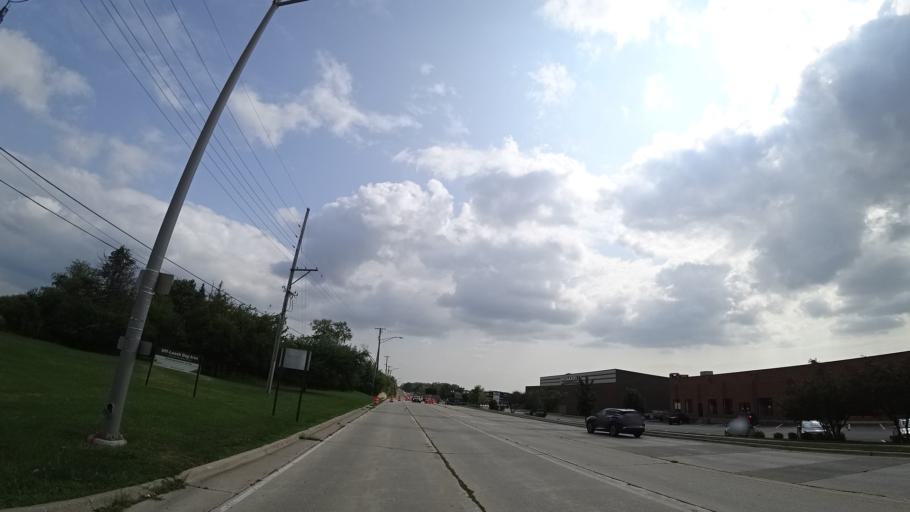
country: US
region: Illinois
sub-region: Cook County
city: Tinley Park
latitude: 41.6010
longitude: -87.7852
